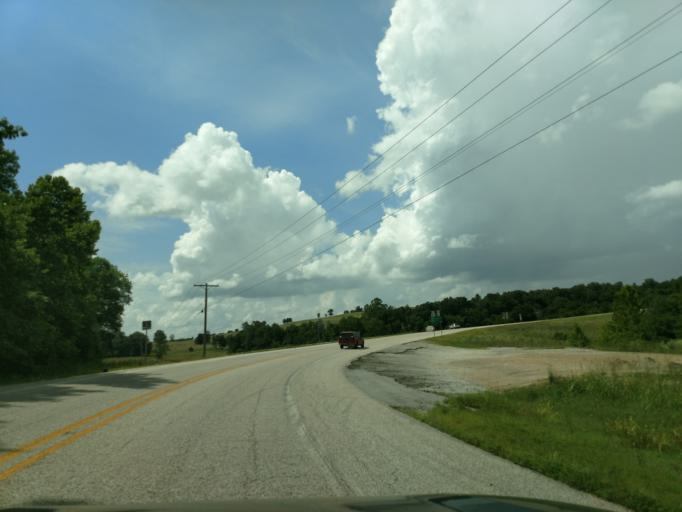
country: US
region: Arkansas
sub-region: Boone County
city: Harrison
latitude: 36.2932
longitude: -93.2419
